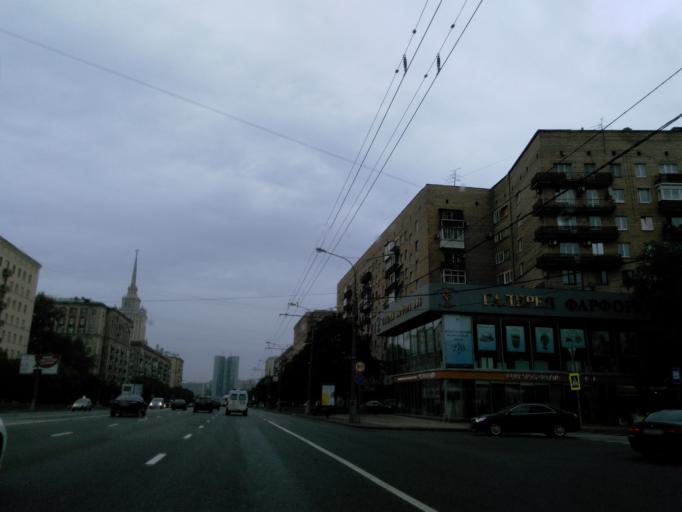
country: RU
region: Moskovskaya
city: Presnenskiy
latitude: 55.7473
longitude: 37.5556
